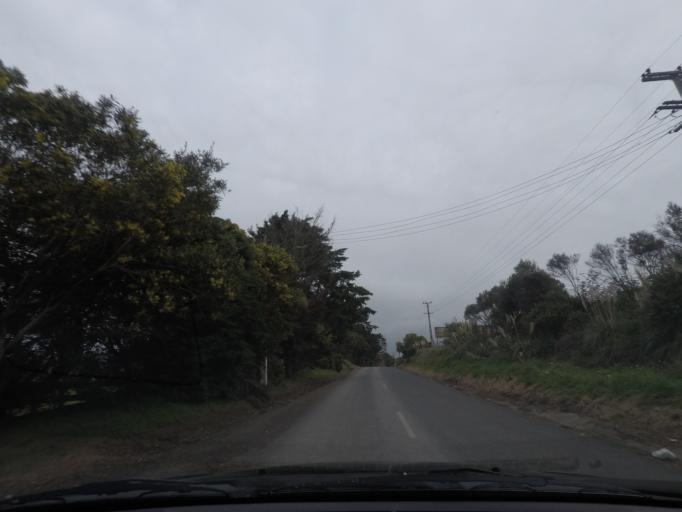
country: NZ
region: Auckland
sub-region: Auckland
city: Muriwai Beach
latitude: -36.7574
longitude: 174.5753
